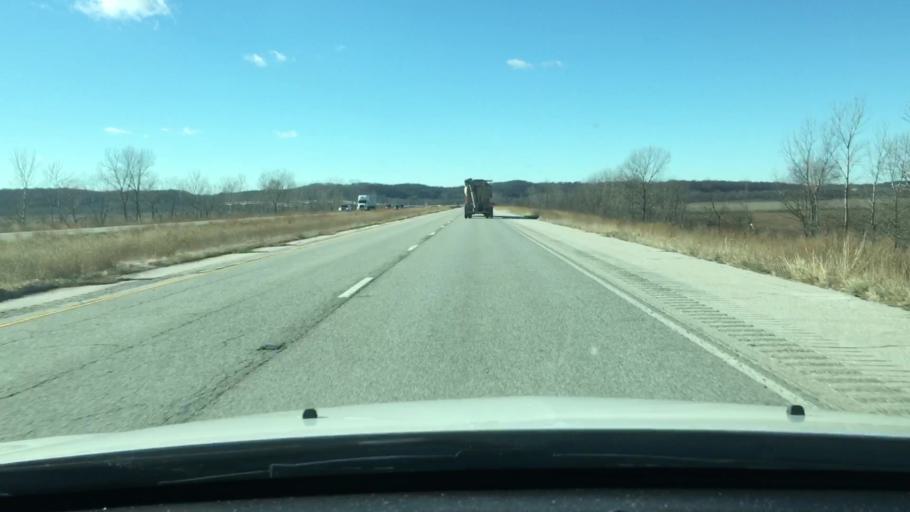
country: US
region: Illinois
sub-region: Pike County
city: Griggsville
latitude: 39.6920
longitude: -90.6143
